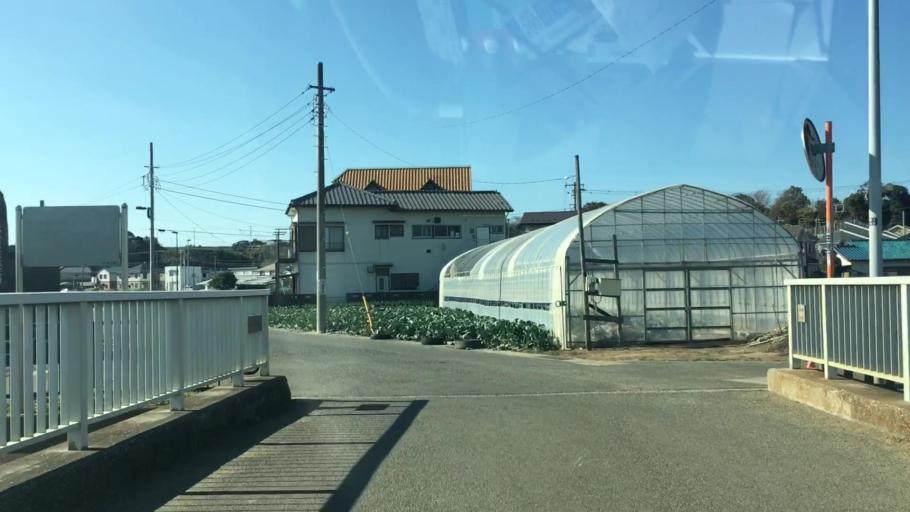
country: JP
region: Kanagawa
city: Miura
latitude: 35.2034
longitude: 139.6223
